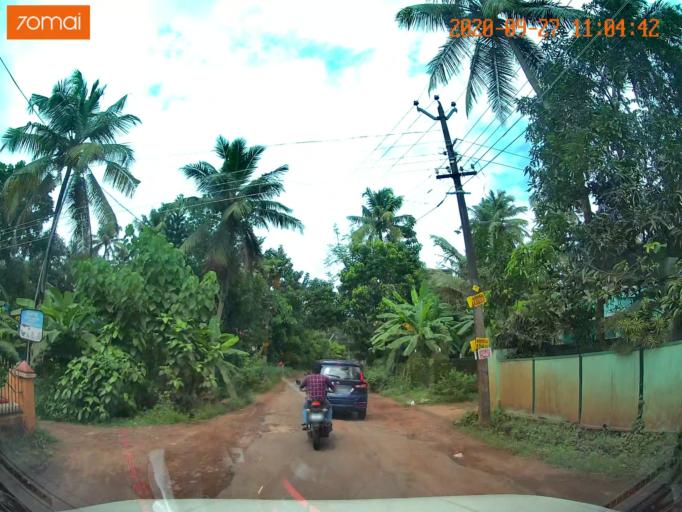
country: IN
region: Kerala
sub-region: Thrissur District
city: Irinjalakuda
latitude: 10.4222
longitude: 76.2505
